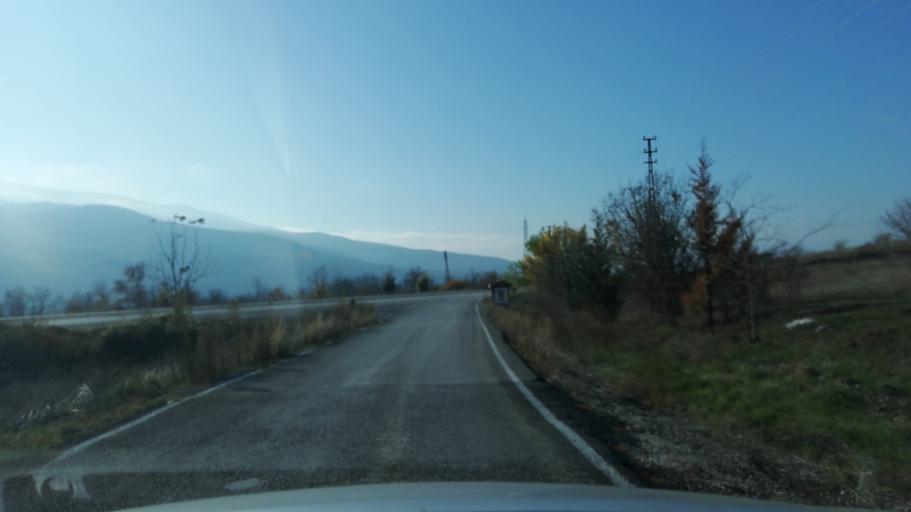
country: TR
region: Karabuk
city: Safranbolu
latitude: 41.2238
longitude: 32.7773
